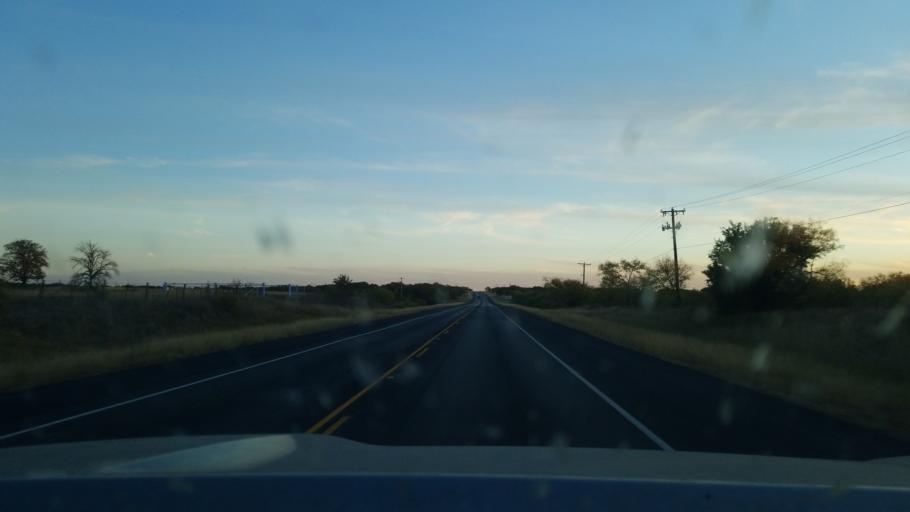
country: US
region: Texas
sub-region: Stephens County
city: Breckenridge
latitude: 32.6942
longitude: -98.9025
